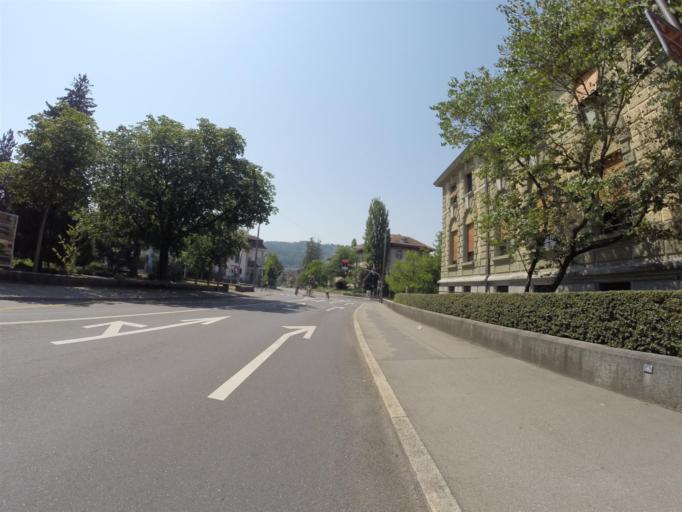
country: CH
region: Bern
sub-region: Bern-Mittelland District
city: Bern
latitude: 46.9406
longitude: 7.4476
